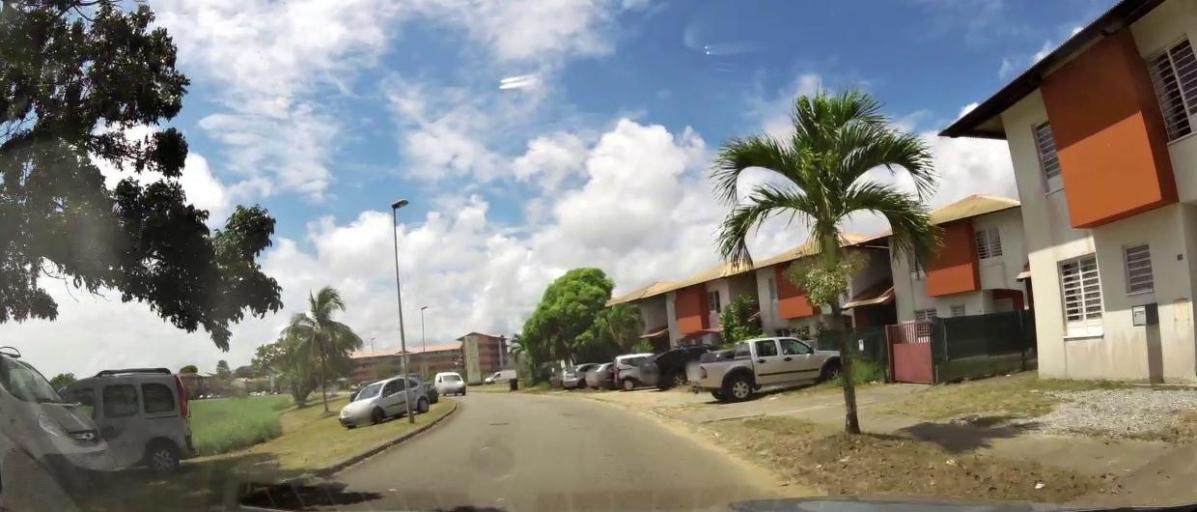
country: GF
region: Guyane
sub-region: Guyane
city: Kourou
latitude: 5.1664
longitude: -52.6532
